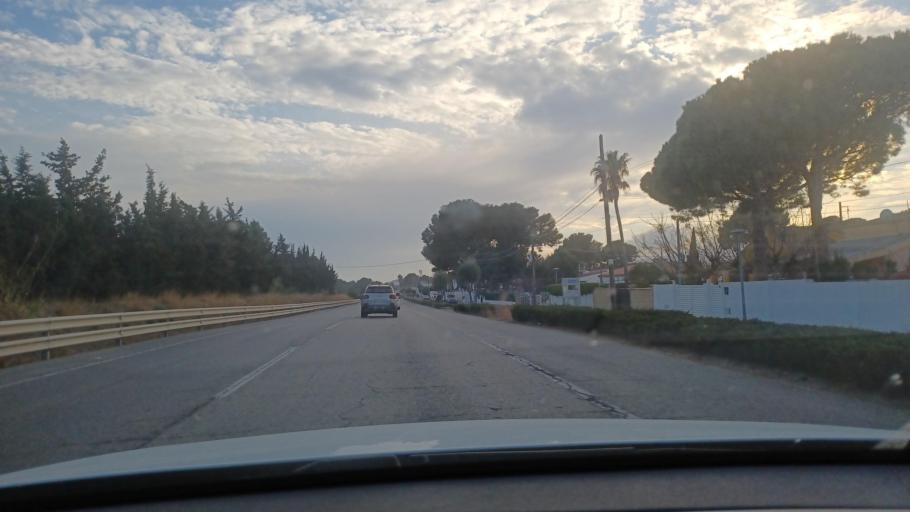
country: ES
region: Catalonia
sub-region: Provincia de Tarragona
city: Vilanova d'Escornalbou
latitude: 41.0328
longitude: 0.9675
